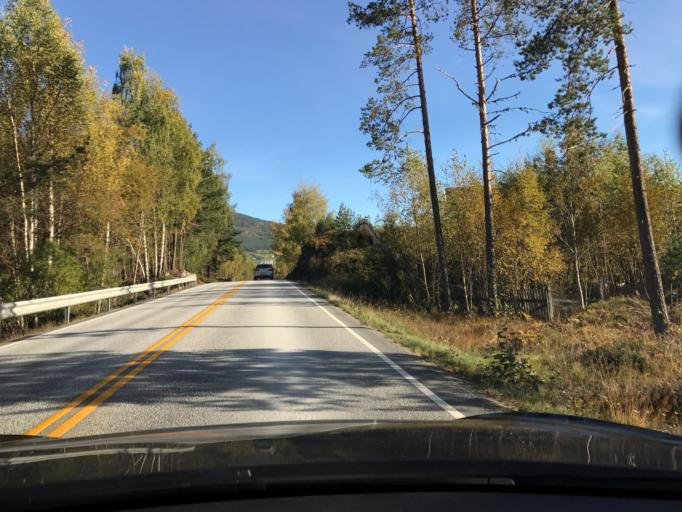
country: NO
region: Sogn og Fjordane
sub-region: Sogndal
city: Sogndalsfjora
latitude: 61.2077
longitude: 7.1862
